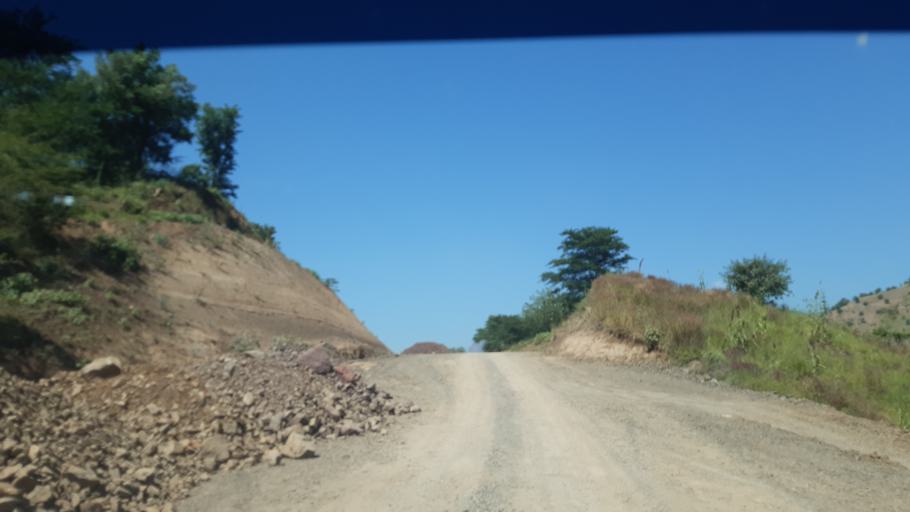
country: ET
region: Amhara
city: Dabat
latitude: 13.1928
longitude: 37.5710
